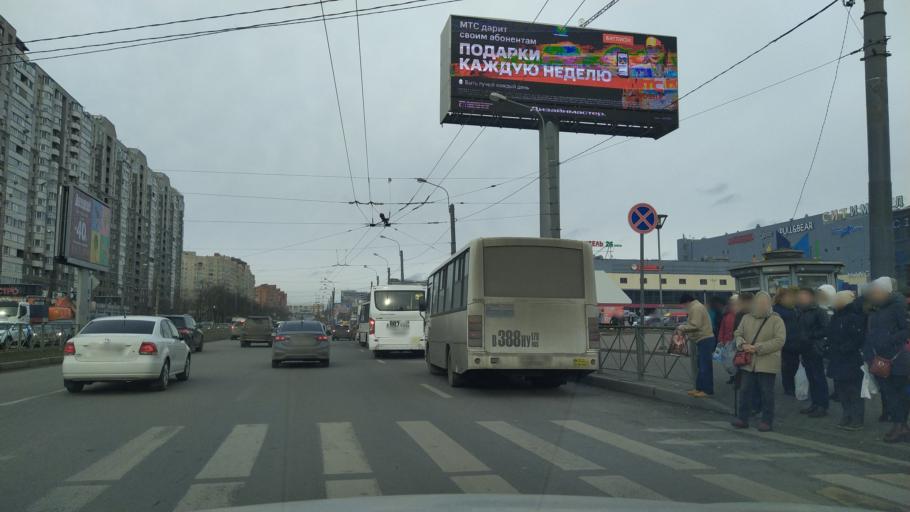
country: RU
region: Leningrad
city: Chernaya Rechka
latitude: 60.0033
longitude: 30.2981
